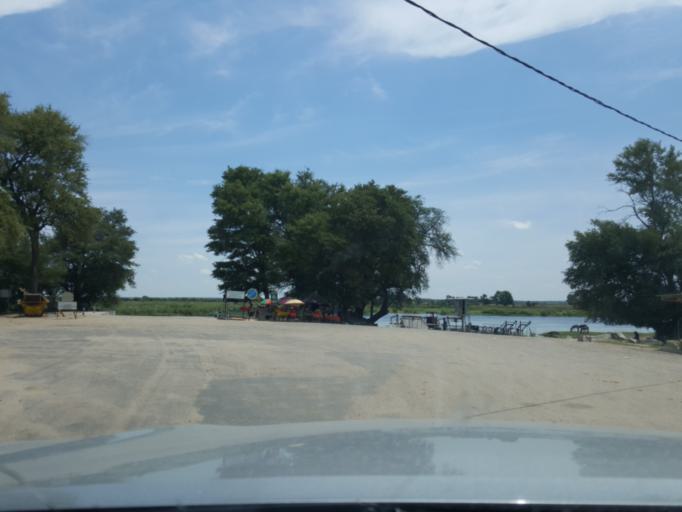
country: BW
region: North West
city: Shakawe
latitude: -18.2771
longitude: 21.7880
